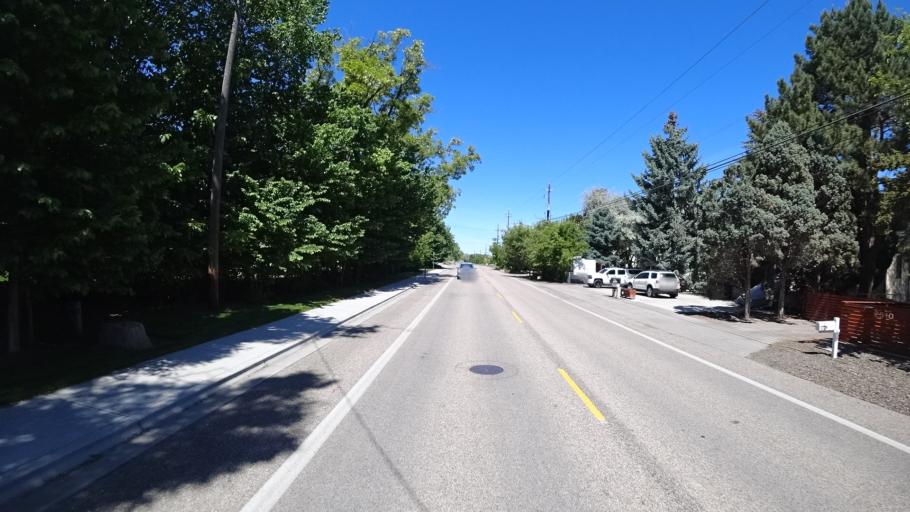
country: US
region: Idaho
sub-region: Ada County
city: Boise
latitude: 43.5706
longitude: -116.1522
